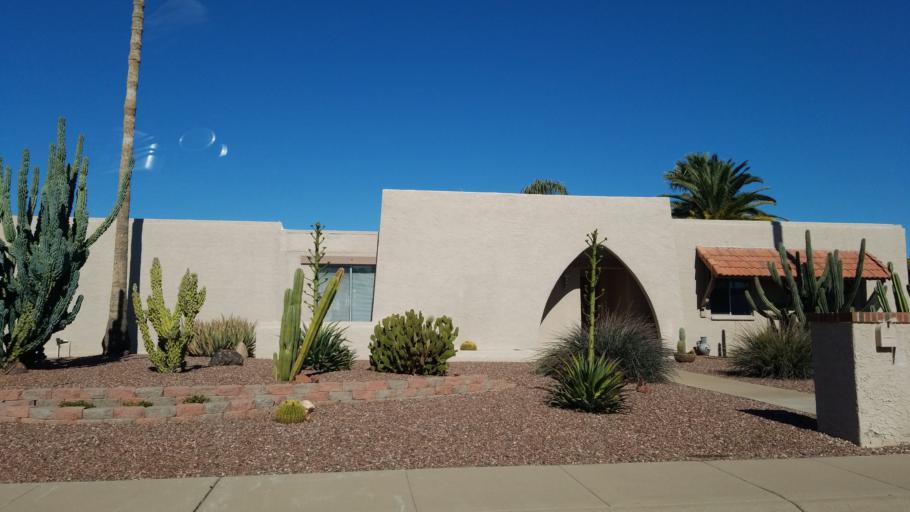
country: US
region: Arizona
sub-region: Maricopa County
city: Paradise Valley
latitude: 33.6135
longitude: -111.9321
